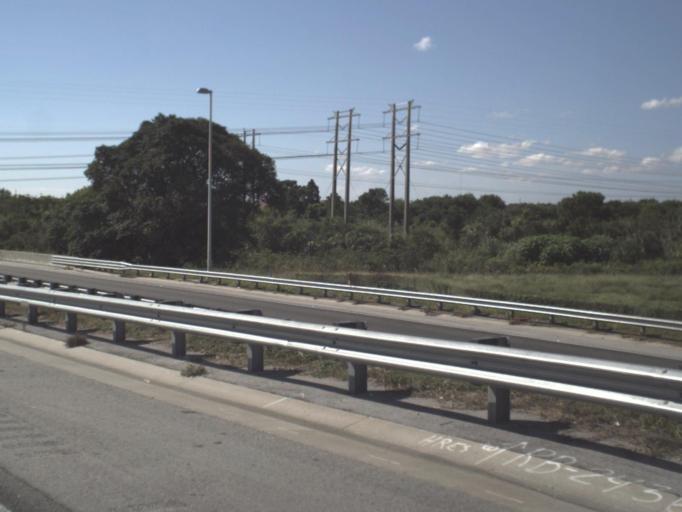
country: US
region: Florida
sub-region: Miami-Dade County
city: Three Lakes
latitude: 25.6467
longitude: -80.3863
